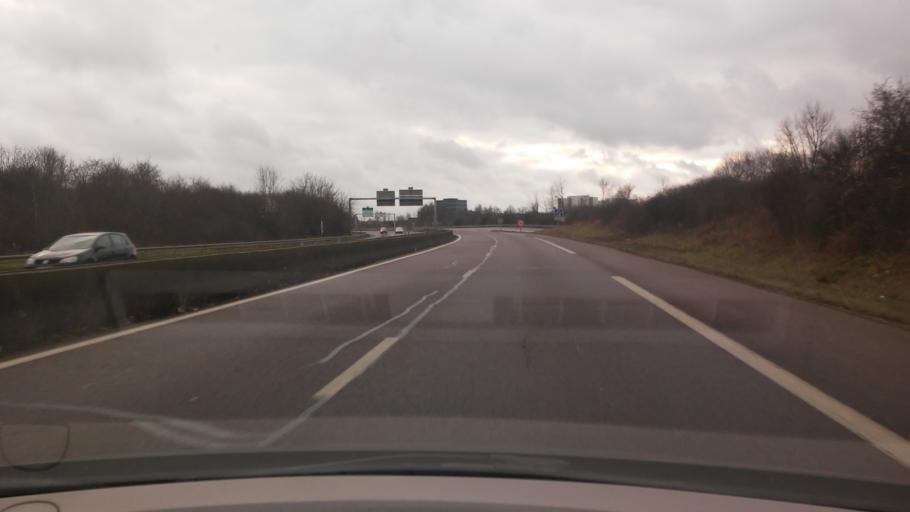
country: FR
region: Lorraine
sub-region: Departement de la Moselle
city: Saint-Julien-les-Metz
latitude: 49.1238
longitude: 6.2370
